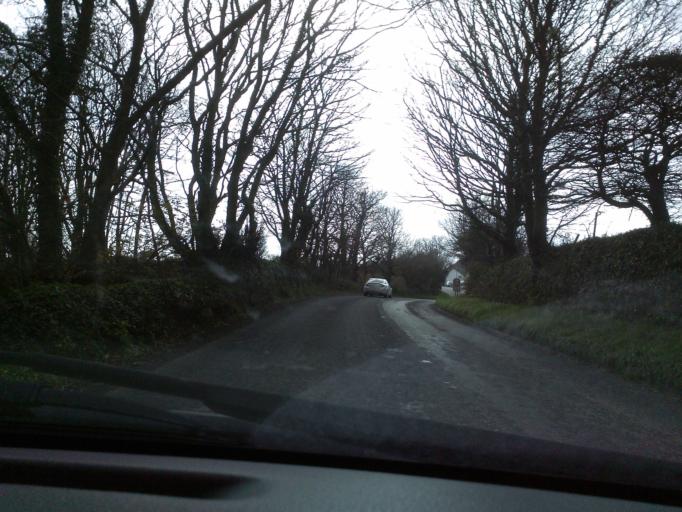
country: GB
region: England
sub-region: Cornwall
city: Penzance
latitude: 50.1031
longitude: -5.5793
